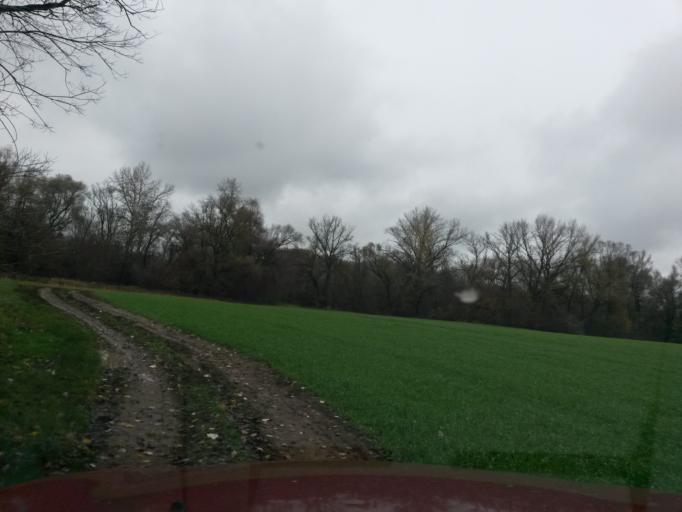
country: SK
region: Kosicky
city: Michalovce
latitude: 48.5628
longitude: 21.9400
